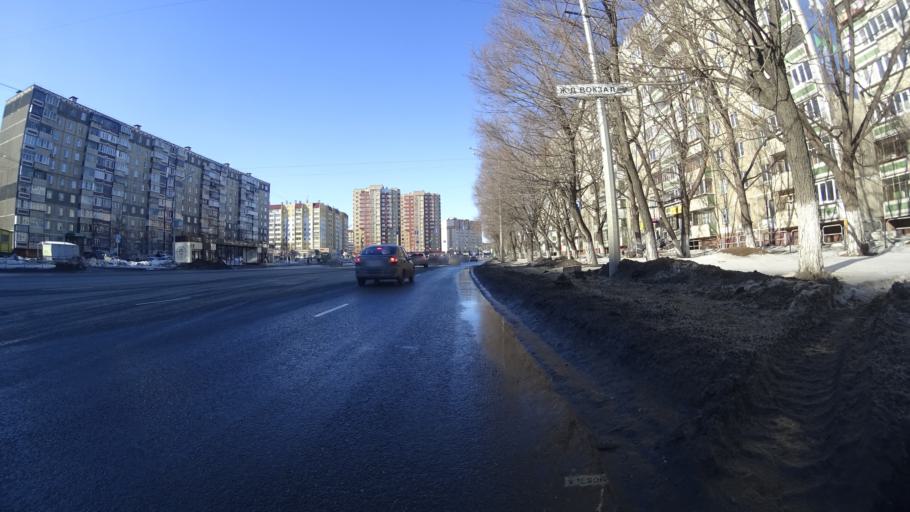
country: RU
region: Chelyabinsk
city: Roshchino
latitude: 55.1899
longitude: 61.2827
